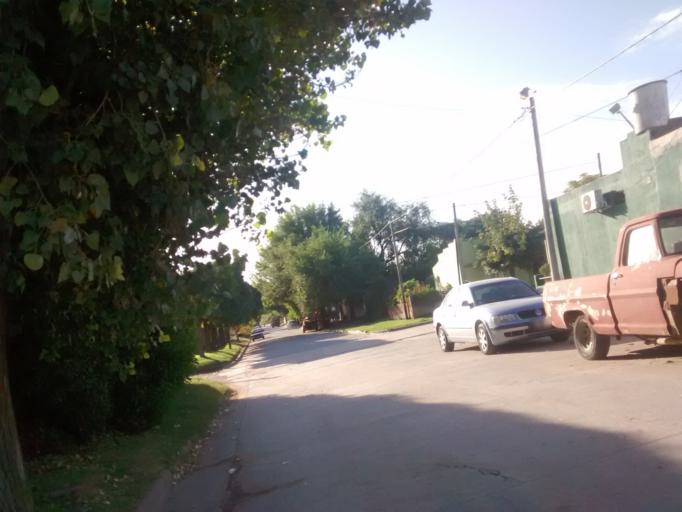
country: AR
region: Buenos Aires
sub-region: Partido de Loberia
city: Loberia
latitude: -38.1702
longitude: -58.7833
